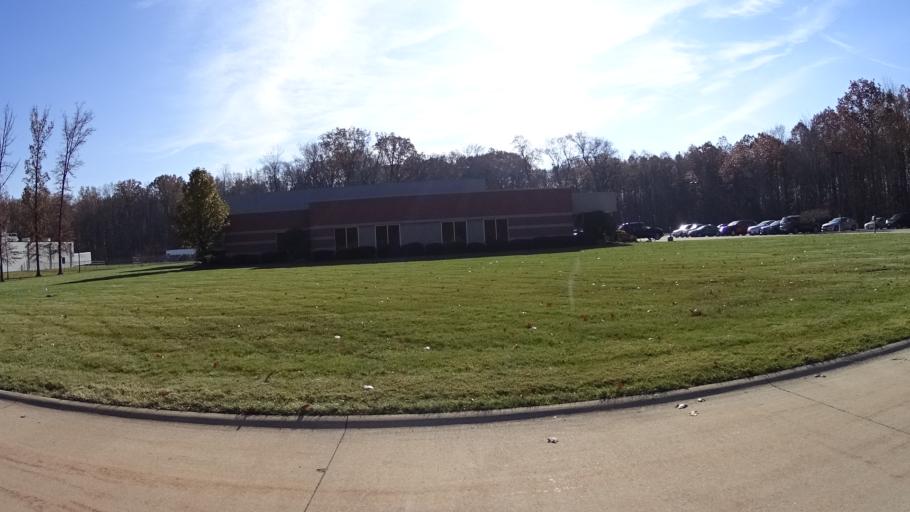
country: US
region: Ohio
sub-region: Lorain County
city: Avon Center
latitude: 41.4769
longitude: -82.0076
